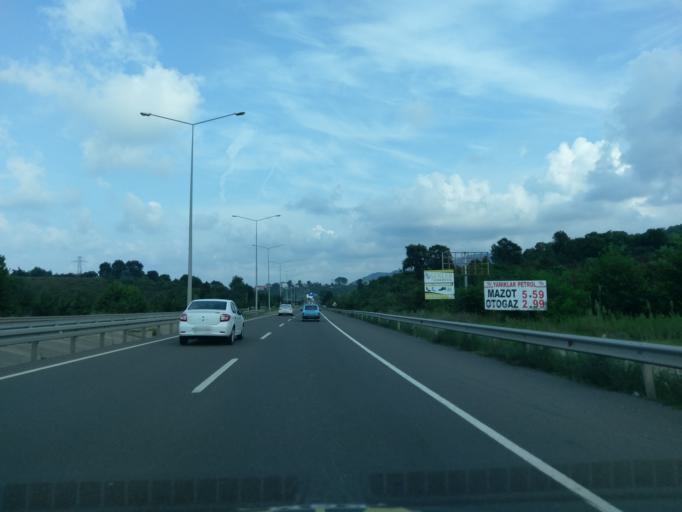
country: TR
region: Ordu
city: Unieh
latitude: 41.1155
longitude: 37.2995
